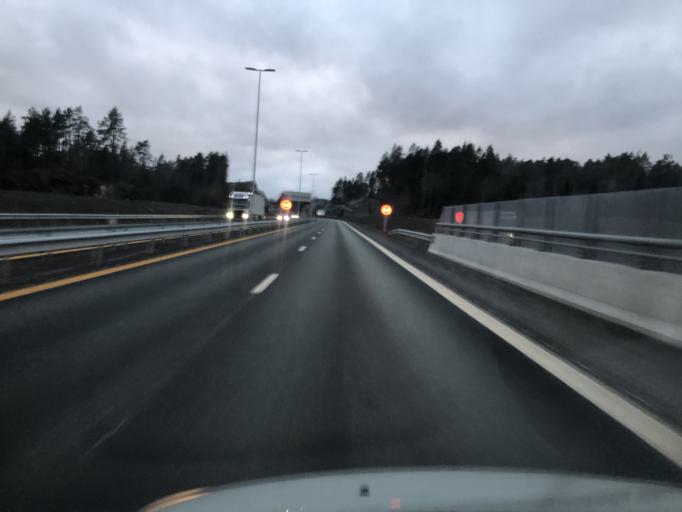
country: NO
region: Aust-Agder
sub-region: Arendal
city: Arendal
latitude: 58.4987
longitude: 8.7832
